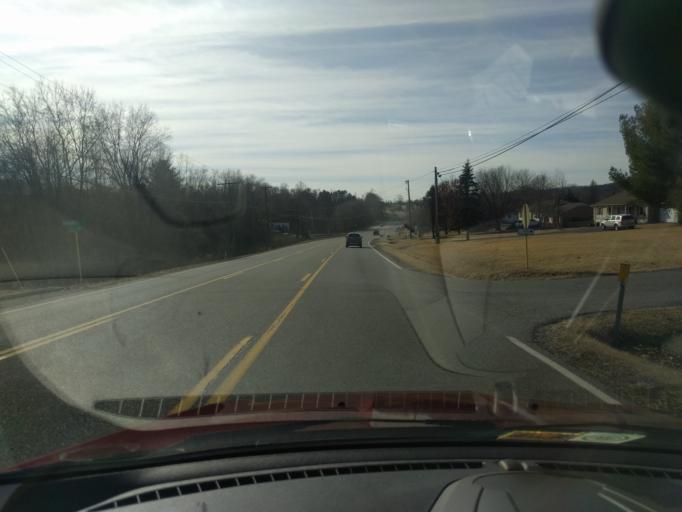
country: US
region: Virginia
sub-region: Augusta County
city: Verona
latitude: 38.2104
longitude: -79.0007
